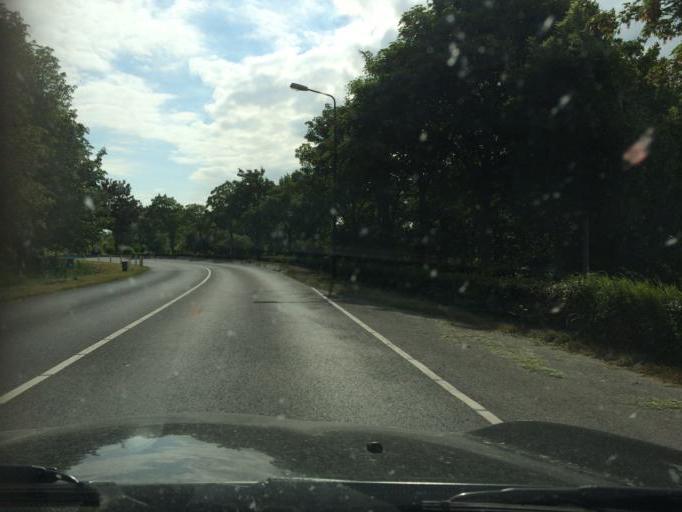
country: NL
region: Utrecht
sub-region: Gemeente Woerden
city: Woerden
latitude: 52.0960
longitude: 4.8933
